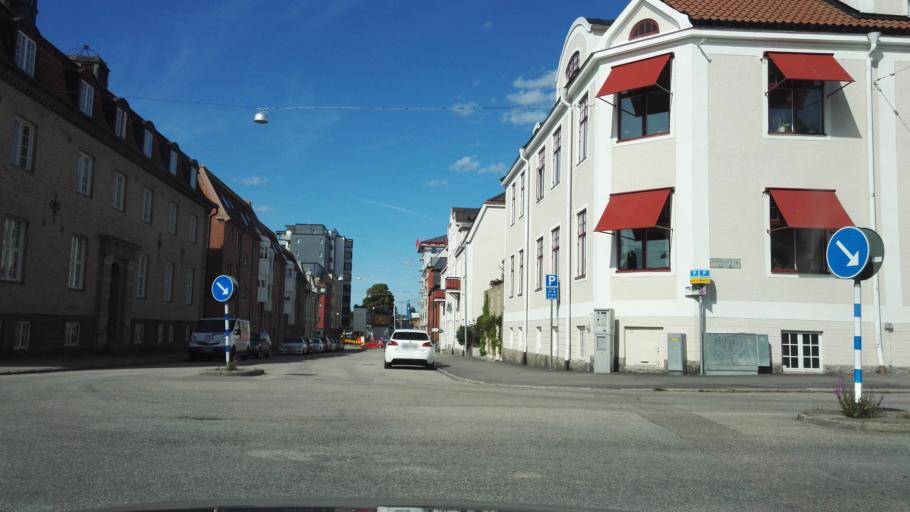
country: SE
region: Kronoberg
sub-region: Vaxjo Kommun
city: Vaexjoe
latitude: 56.8746
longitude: 14.8028
